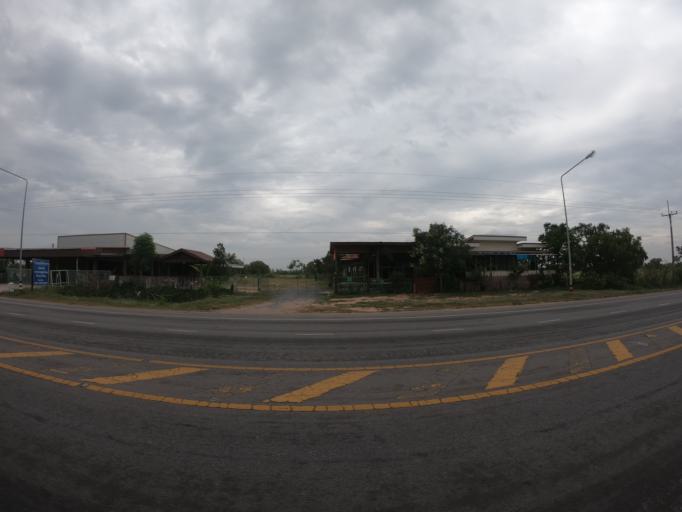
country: TH
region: Roi Et
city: Thawat Buri
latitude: 16.0915
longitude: 103.7746
